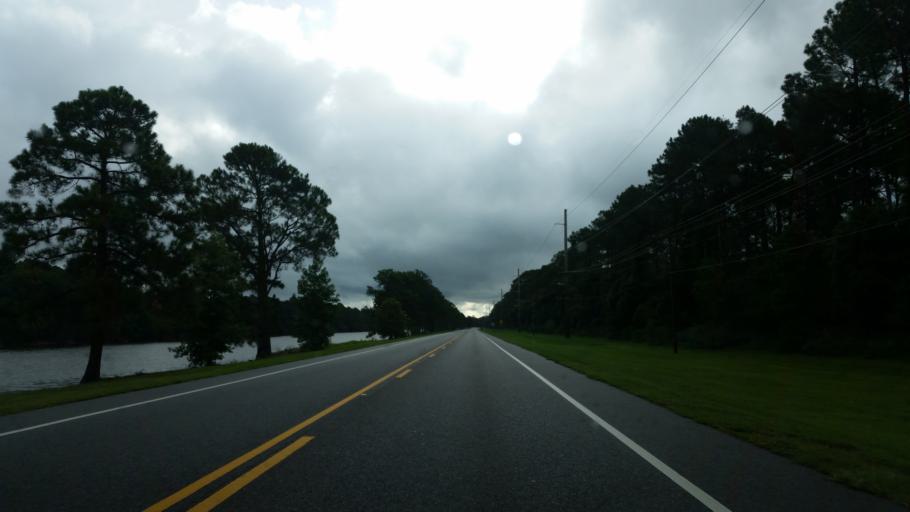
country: US
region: Alabama
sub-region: Baldwin County
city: Gulf Shores
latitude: 30.2793
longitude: -87.6651
